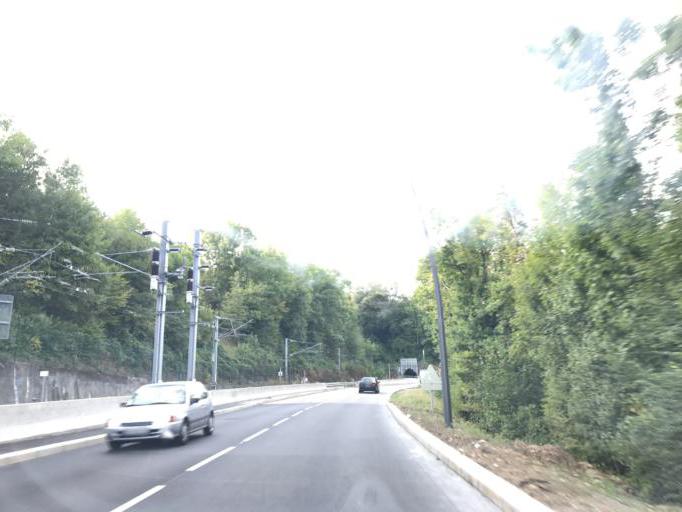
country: FR
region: Rhone-Alpes
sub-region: Departement de l'Ain
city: Bellegarde-sur-Valserine
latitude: 46.1147
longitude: 5.8233
